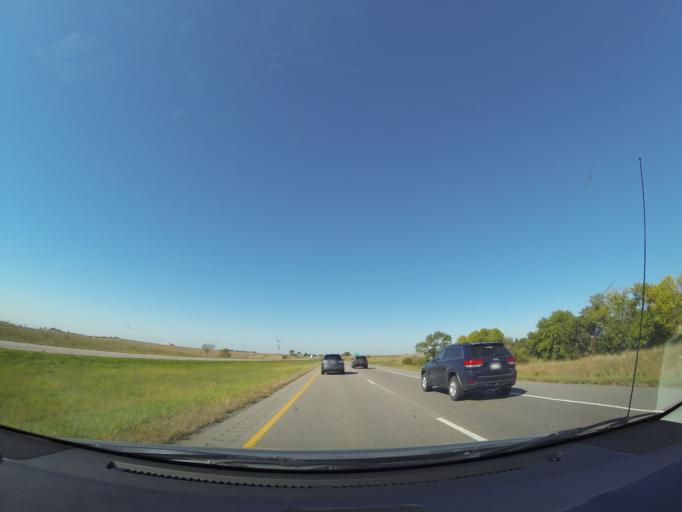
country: US
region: Nebraska
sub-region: Saline County
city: Friend
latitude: 40.8218
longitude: -97.3198
